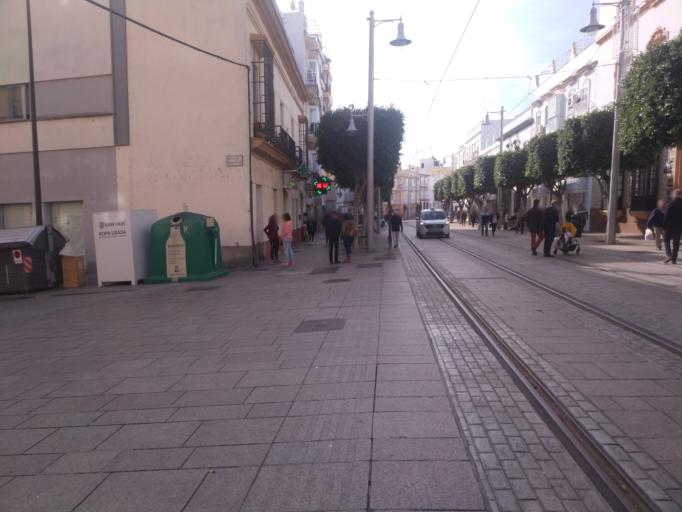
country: ES
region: Andalusia
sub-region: Provincia de Cadiz
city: San Fernando
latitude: 36.4598
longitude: -6.2015
